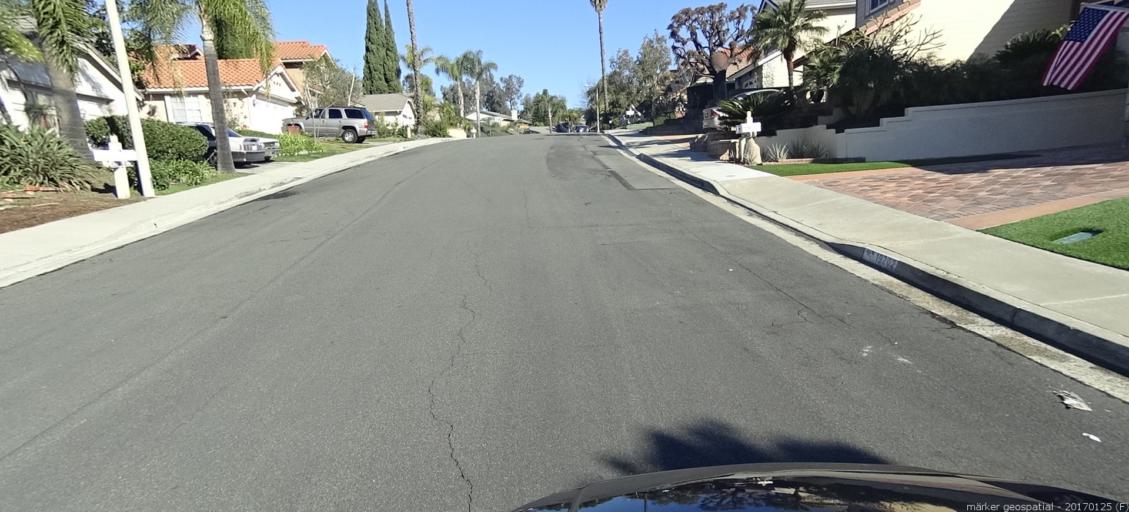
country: US
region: California
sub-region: Orange County
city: Portola Hills
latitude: 33.6829
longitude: -117.6291
